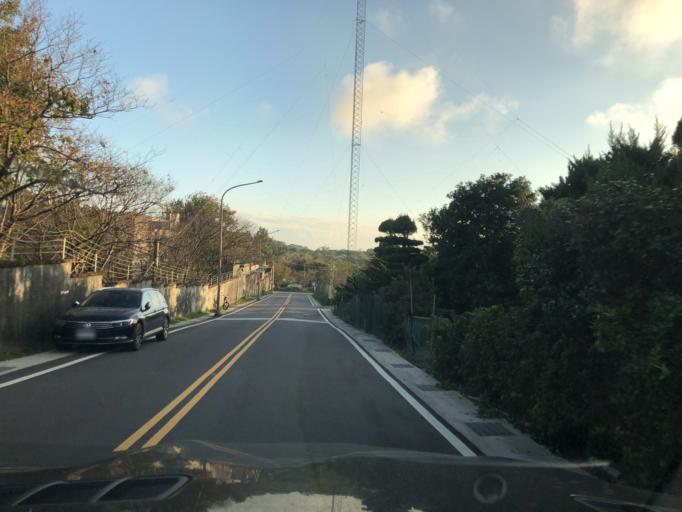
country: TW
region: Taipei
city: Taipei
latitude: 25.1450
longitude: 121.5576
